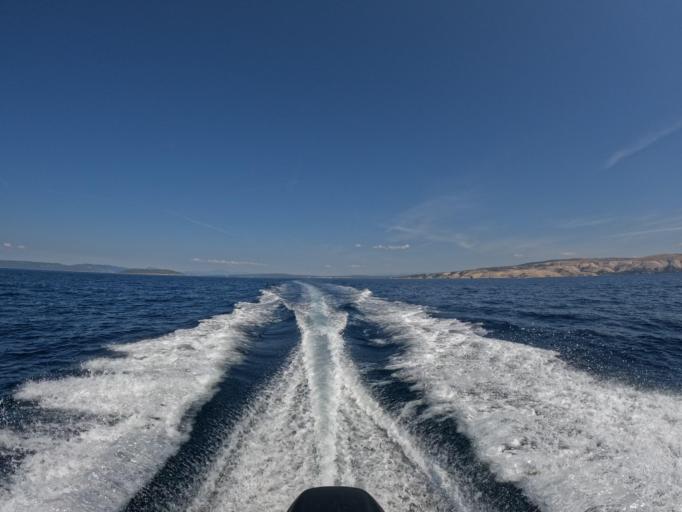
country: HR
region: Primorsko-Goranska
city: Punat
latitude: 44.9135
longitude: 14.6264
